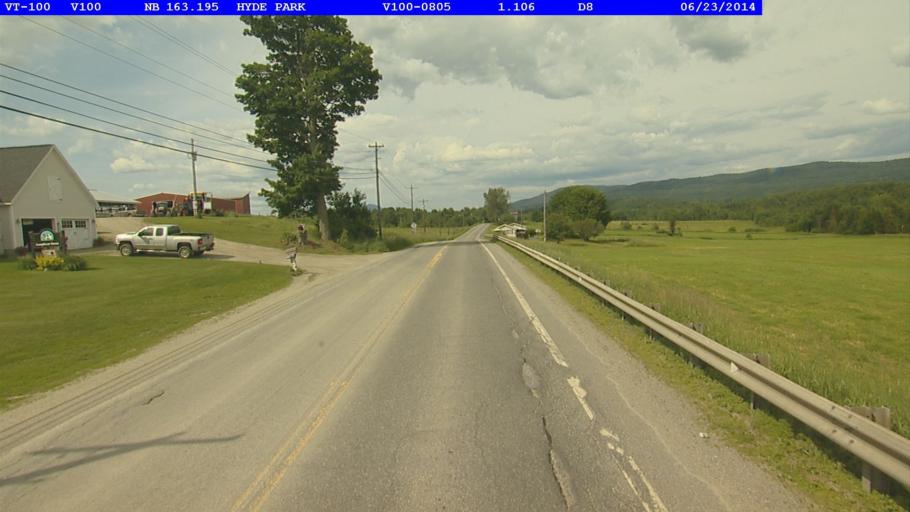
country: US
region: Vermont
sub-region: Lamoille County
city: Hyde Park
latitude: 44.6120
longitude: -72.6079
